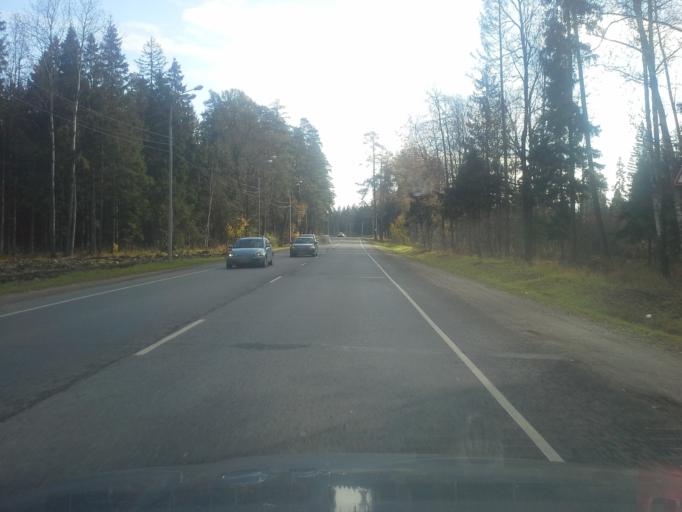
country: RU
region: Moskovskaya
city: Bol'shiye Vyazemy
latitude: 55.6751
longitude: 36.9337
